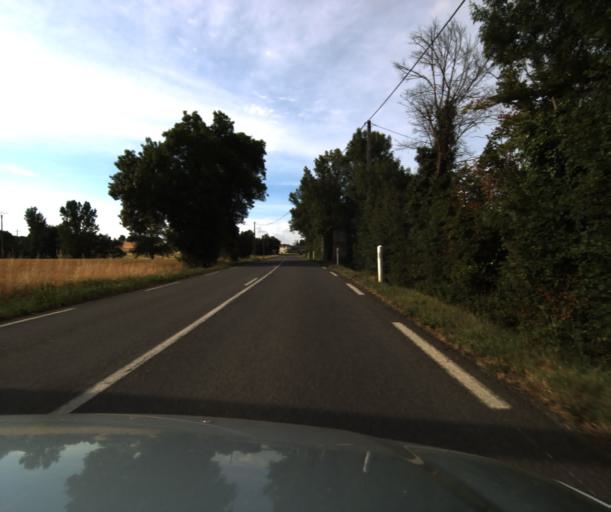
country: FR
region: Midi-Pyrenees
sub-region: Departement du Tarn-et-Garonne
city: Beaumont-de-Lomagne
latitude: 43.7963
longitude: 0.8944
